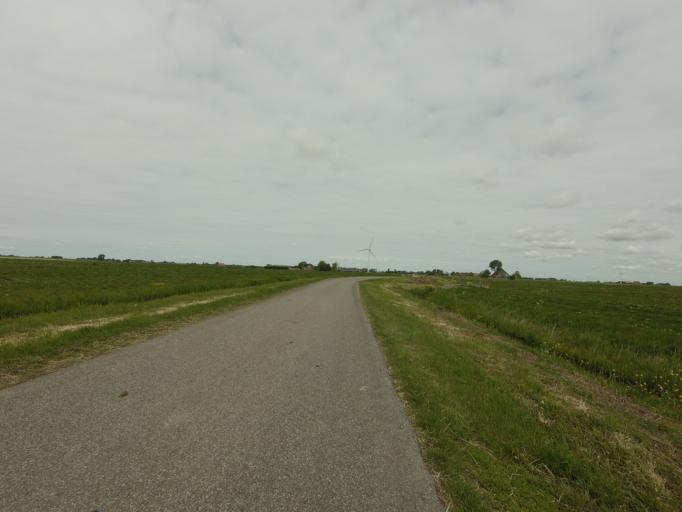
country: NL
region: Friesland
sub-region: Sudwest Fryslan
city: Workum
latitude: 52.9547
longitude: 5.4702
